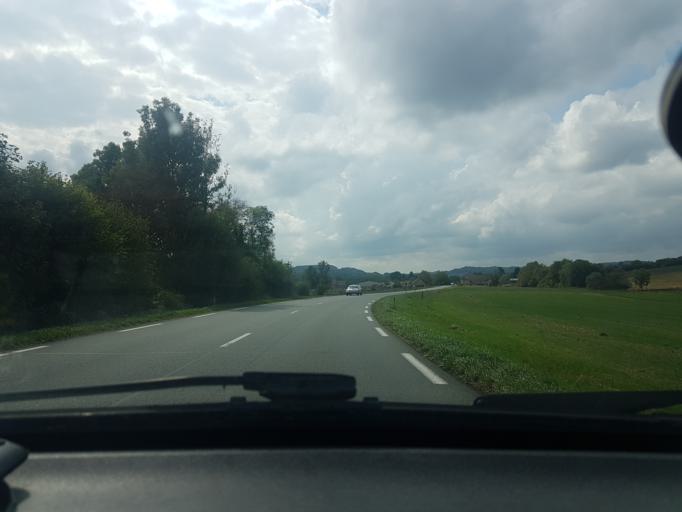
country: FR
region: Franche-Comte
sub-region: Departement du Doubs
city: Arcey
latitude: 47.5544
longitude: 6.5939
